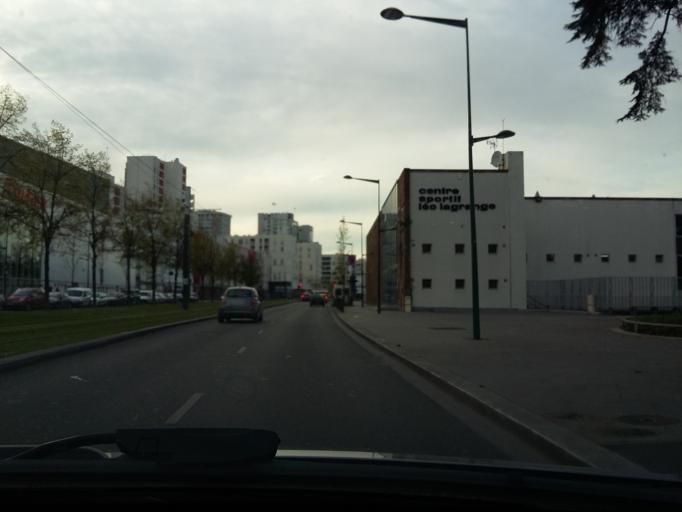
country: FR
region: Ile-de-France
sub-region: Departement de Seine-Saint-Denis
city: Epinay-sur-Seine
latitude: 48.9537
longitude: 2.3147
